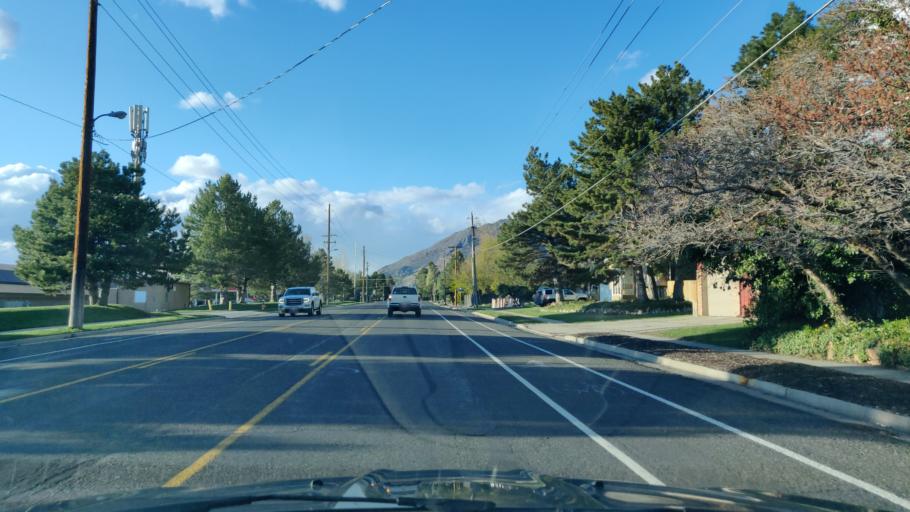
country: US
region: Utah
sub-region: Salt Lake County
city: Cottonwood Heights
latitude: 40.6073
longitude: -111.7959
